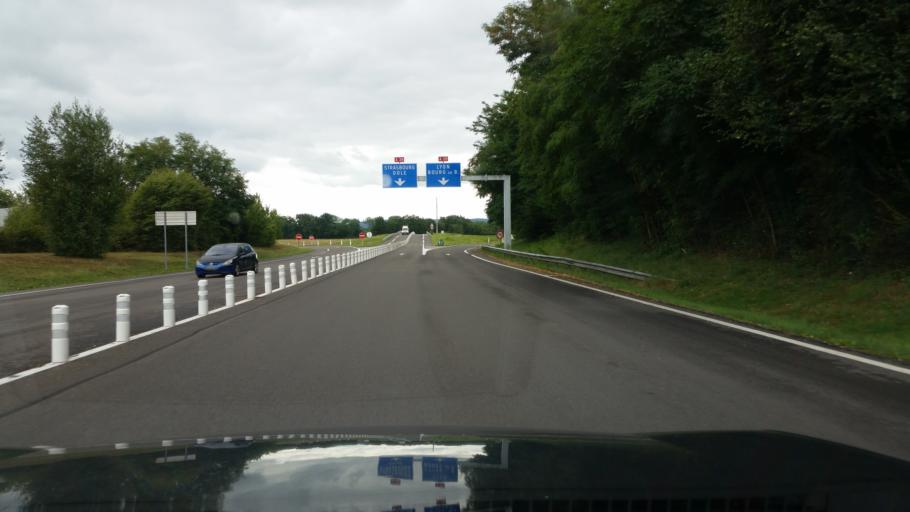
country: FR
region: Franche-Comte
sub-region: Departement du Jura
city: Bletterans
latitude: 46.6661
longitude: 5.4201
